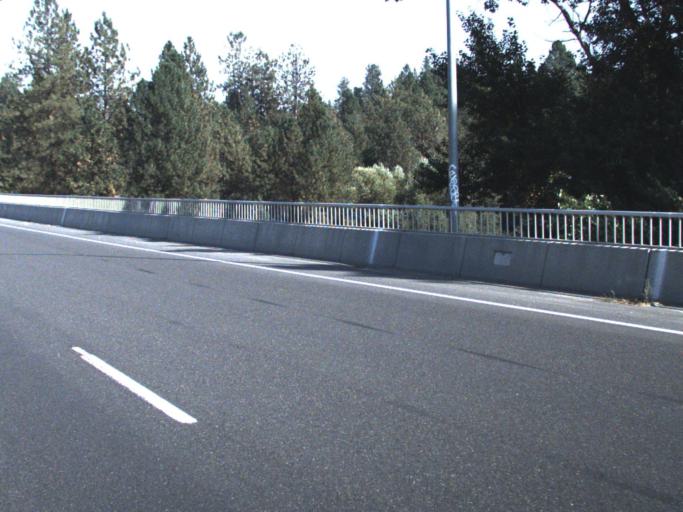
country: US
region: Washington
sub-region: Spokane County
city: Mead
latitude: 47.7782
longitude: -117.3654
